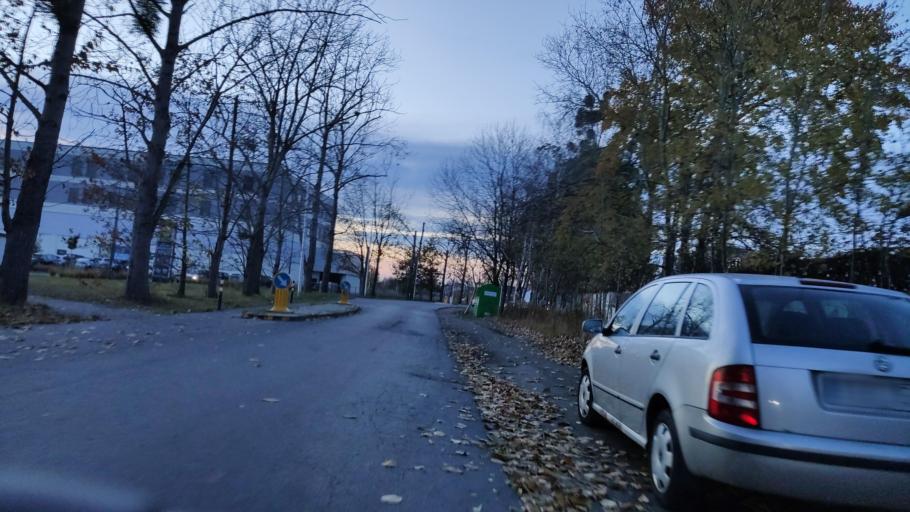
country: PL
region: Lower Silesian Voivodeship
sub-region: Powiat wroclawski
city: Zerniki Wroclawskie
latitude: 51.0690
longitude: 17.0569
